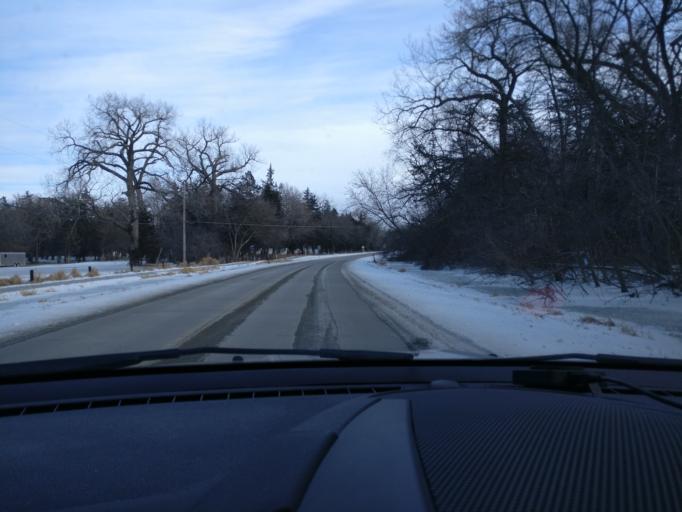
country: US
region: Nebraska
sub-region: Dodge County
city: Fremont
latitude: 41.4131
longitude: -96.5172
